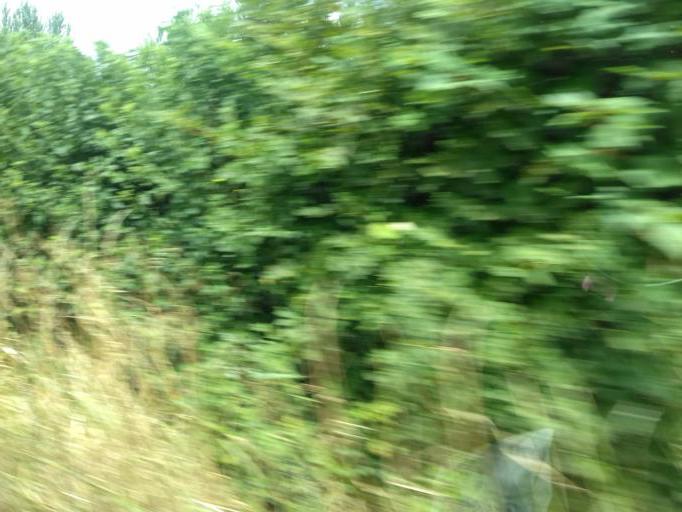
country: IE
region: Leinster
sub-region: Kilkenny
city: Graiguenamanagh
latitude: 52.5906
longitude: -6.9676
